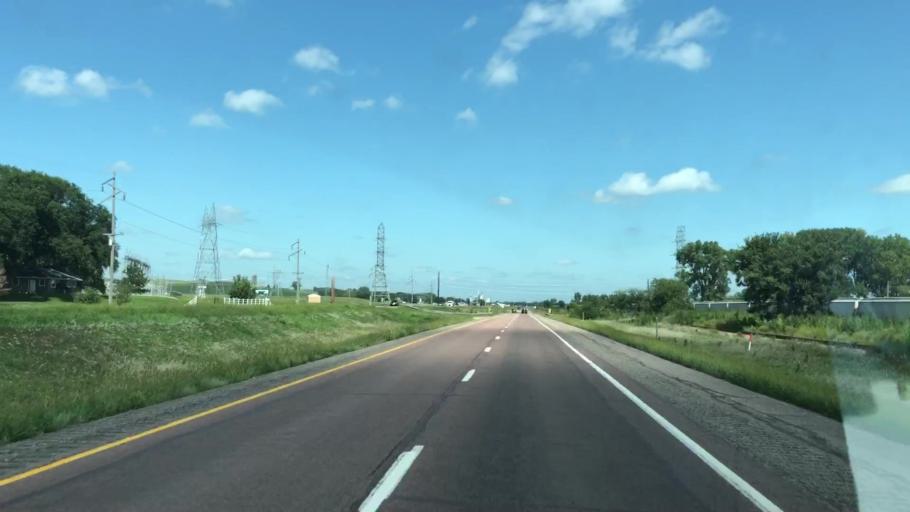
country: US
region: Iowa
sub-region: Woodbury County
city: Sioux City
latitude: 42.5962
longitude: -96.3039
